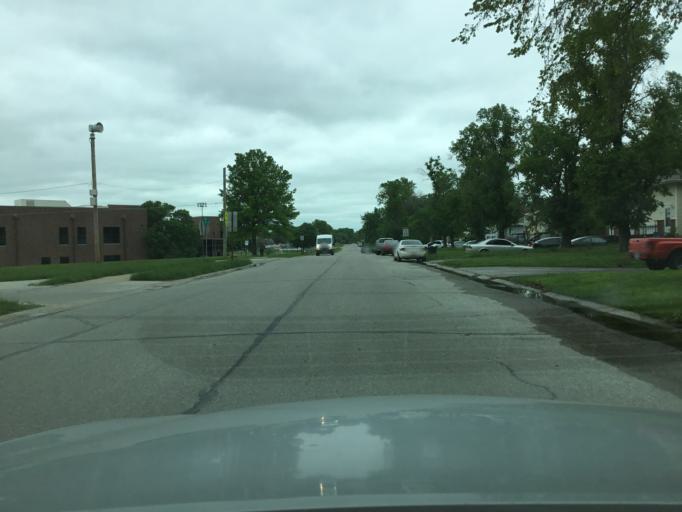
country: US
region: Kansas
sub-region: Franklin County
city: Ottawa
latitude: 38.5968
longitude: -95.2770
